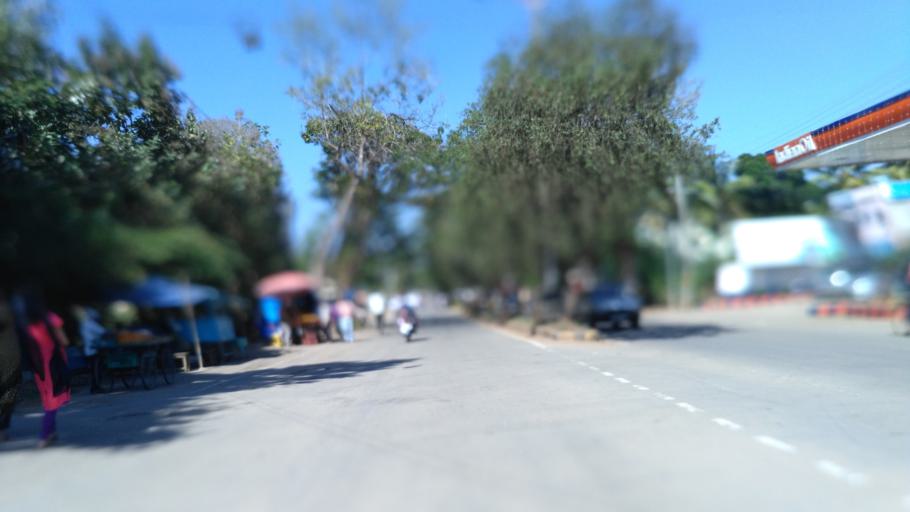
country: IN
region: Karnataka
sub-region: Hassan
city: Hassan
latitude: 13.0133
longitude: 76.1059
